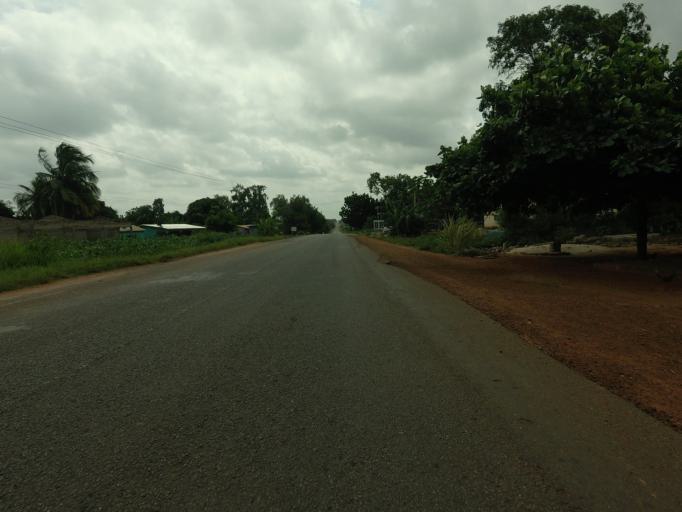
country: TG
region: Maritime
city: Lome
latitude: 6.1382
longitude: 1.1148
